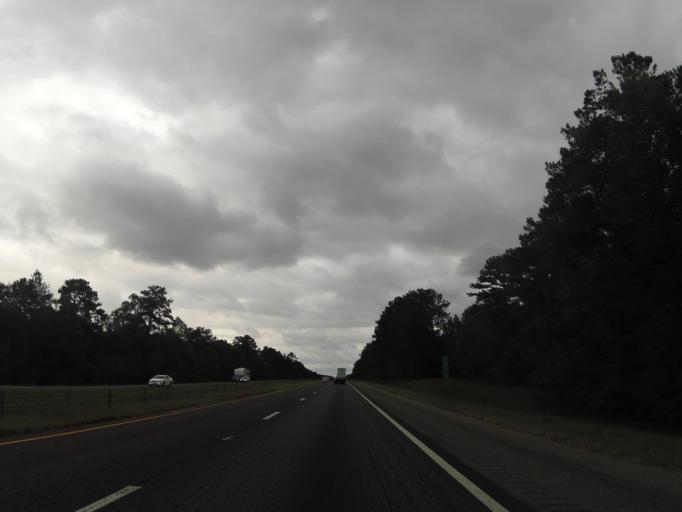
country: US
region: Alabama
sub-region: Butler County
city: Georgiana
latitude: 31.6183
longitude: -86.8082
